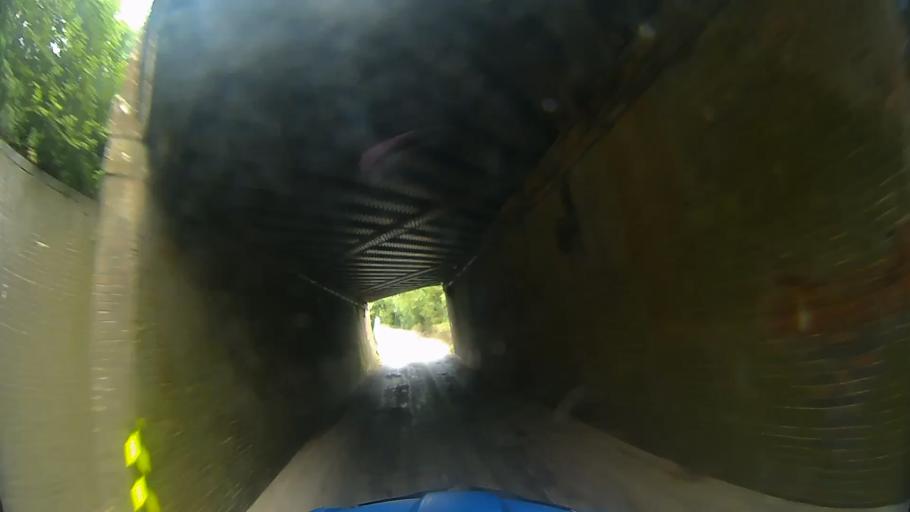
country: GB
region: England
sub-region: Hampshire
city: Basingstoke
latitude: 51.2540
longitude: -1.1540
